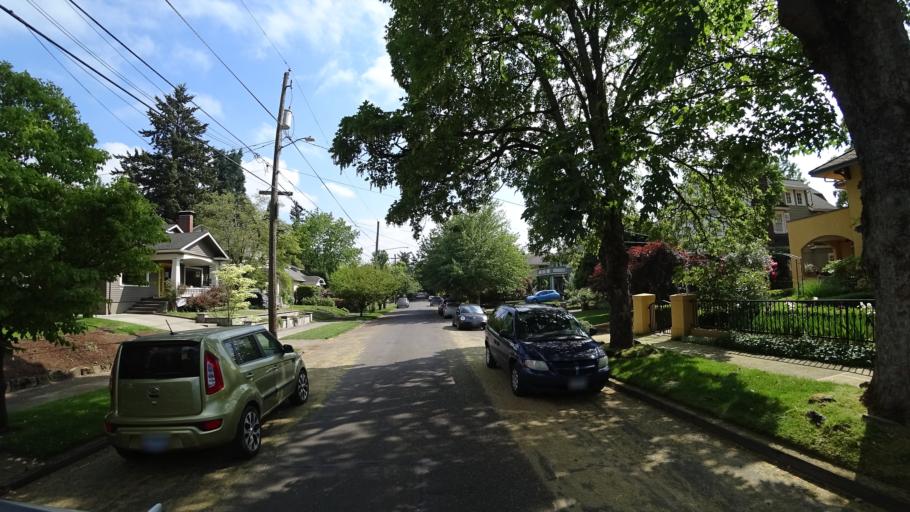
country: US
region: Oregon
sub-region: Multnomah County
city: Portland
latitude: 45.5475
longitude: -122.6463
